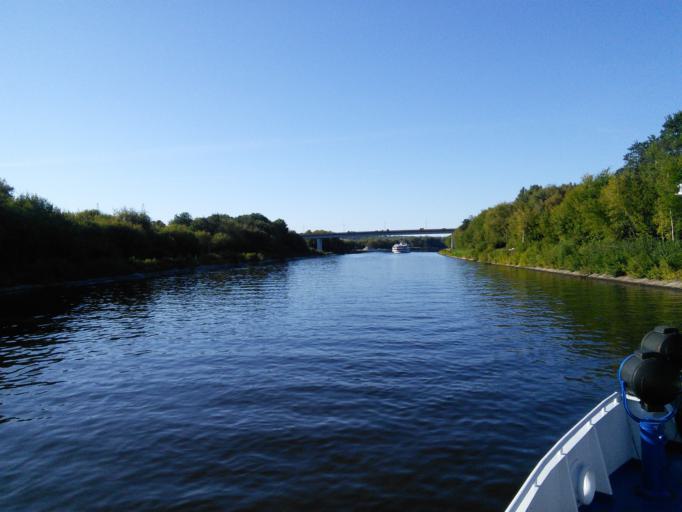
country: RU
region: Moskovskaya
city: Yakhroma
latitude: 56.2906
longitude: 37.4949
